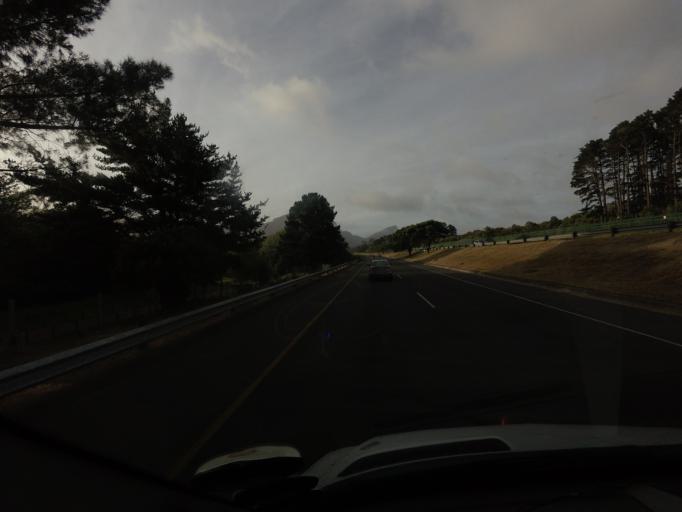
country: ZA
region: Western Cape
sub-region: City of Cape Town
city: Claremont
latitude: -34.0119
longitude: 18.4532
